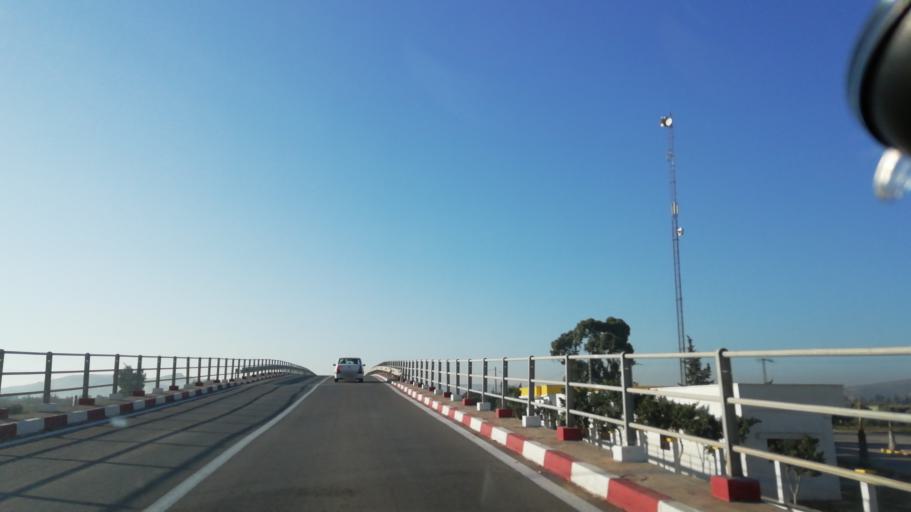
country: DZ
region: Tlemcen
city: Remchi
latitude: 35.0481
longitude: -1.5034
